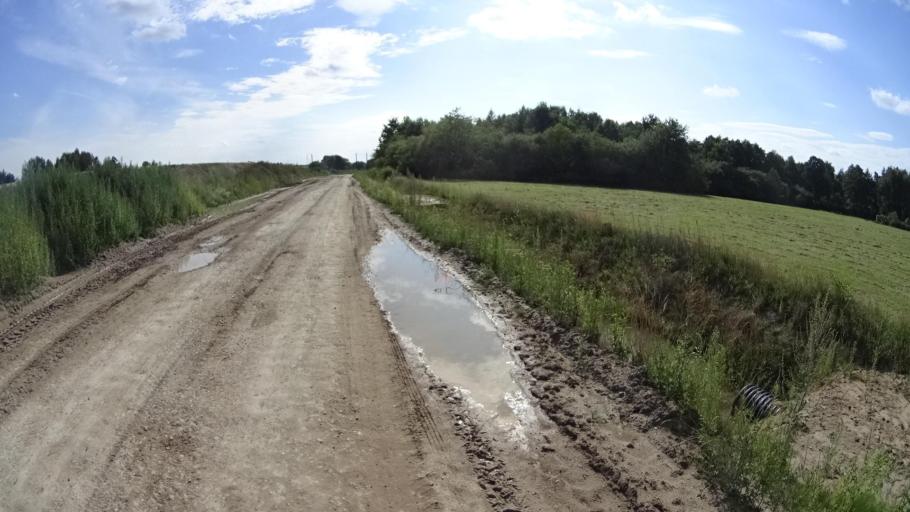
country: PL
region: Masovian Voivodeship
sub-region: Powiat piaseczynski
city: Lesznowola
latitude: 52.0569
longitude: 20.9268
